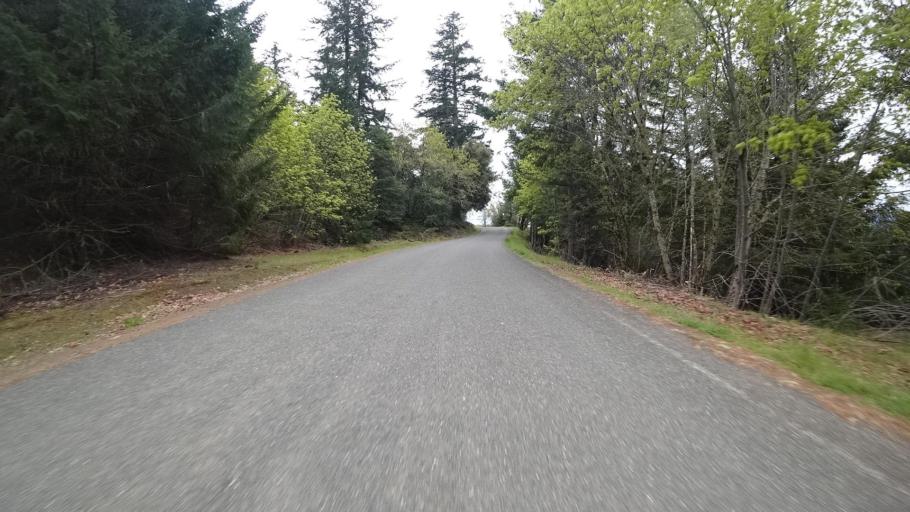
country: US
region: California
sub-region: Humboldt County
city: Redway
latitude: 40.1571
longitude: -123.5577
